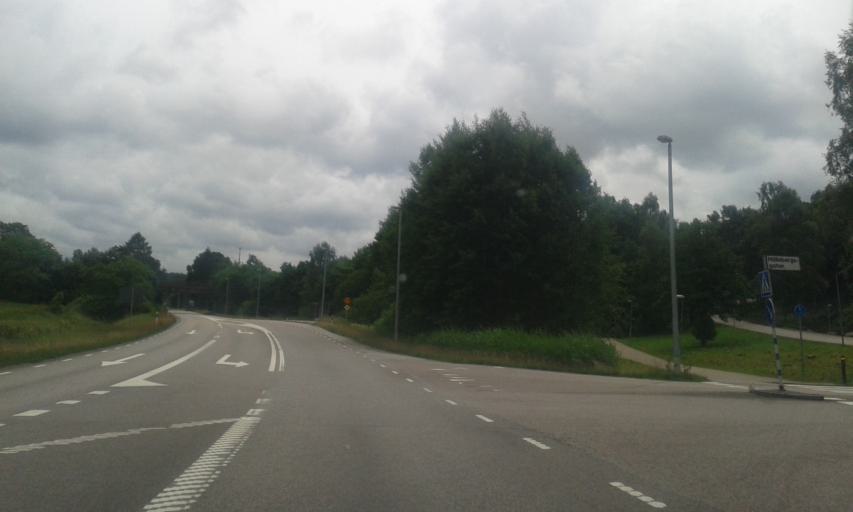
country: SE
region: Vaestra Goetaland
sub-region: Kungalvs Kommun
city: Kungalv
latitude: 57.8676
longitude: 11.9159
